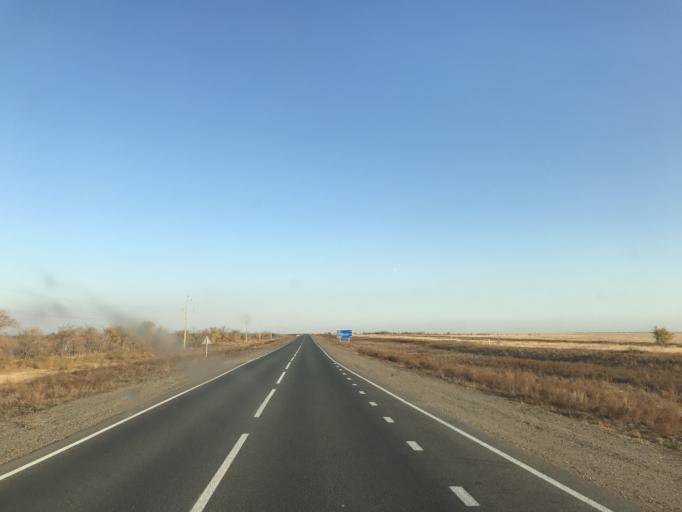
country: KZ
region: Pavlodar
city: Kurchatov
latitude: 51.0341
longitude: 79.1312
